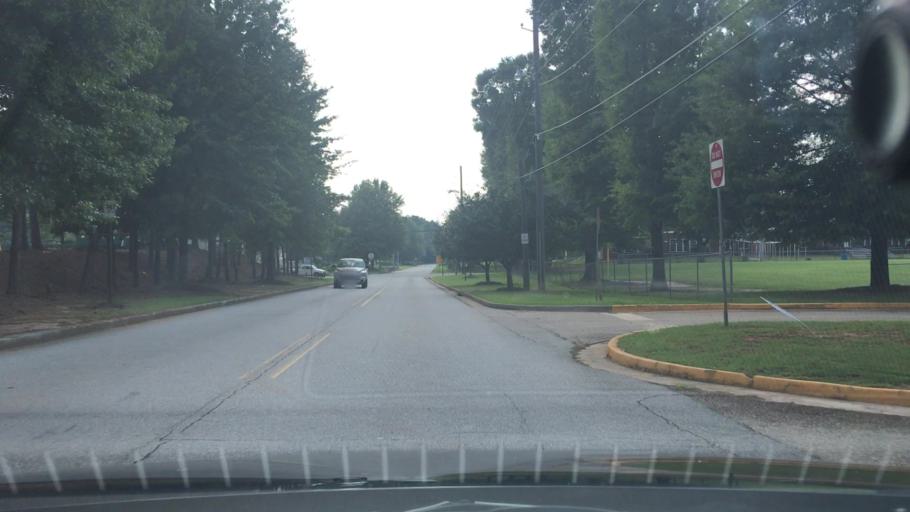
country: US
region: Georgia
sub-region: Spalding County
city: Experiment
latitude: 33.2501
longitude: -84.2895
